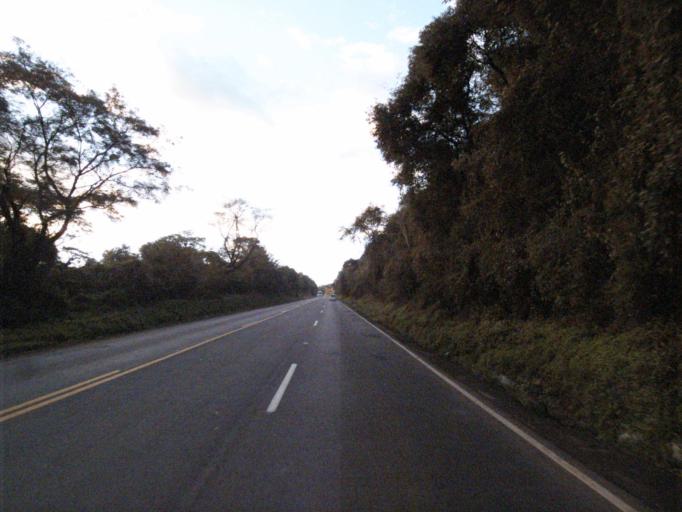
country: BR
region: Santa Catarina
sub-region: Joacaba
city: Joacaba
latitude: -27.1886
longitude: -51.5179
